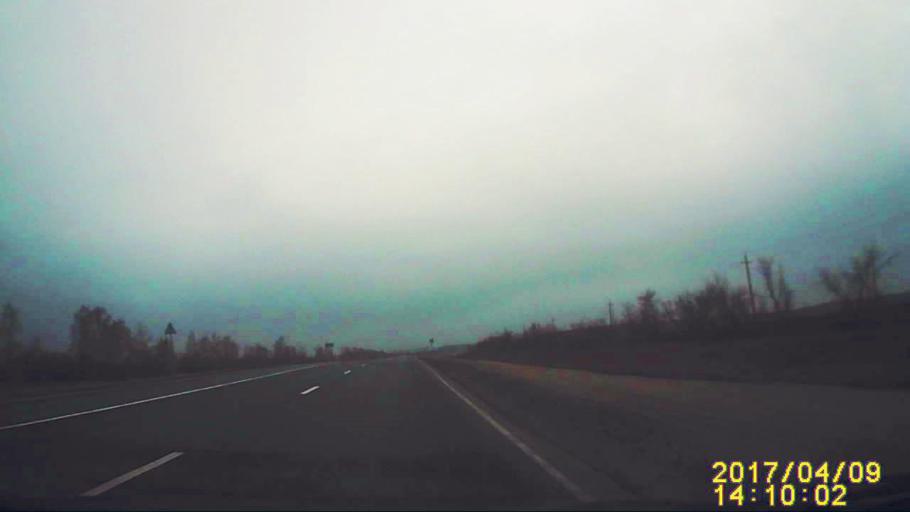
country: RU
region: Ulyanovsk
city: Krasnyy Gulyay
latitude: 54.0342
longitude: 48.2130
